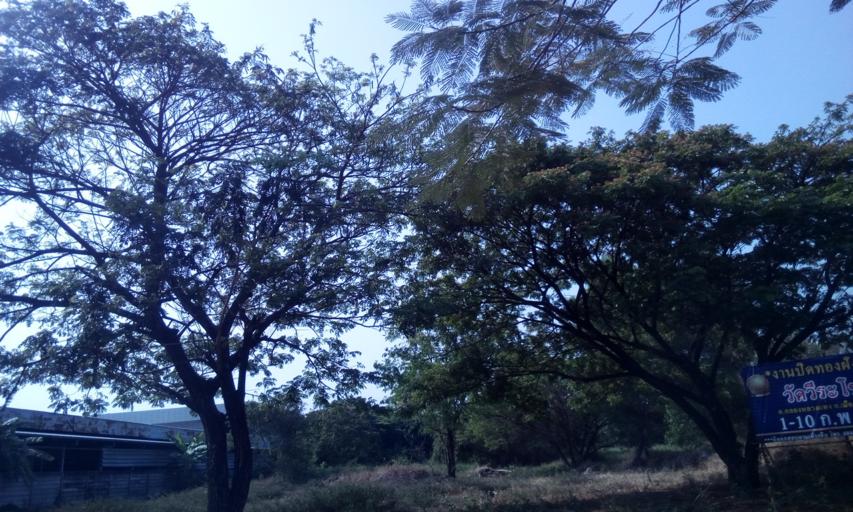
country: TH
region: Bangkok
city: Sai Mai
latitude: 13.9331
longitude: 100.6951
